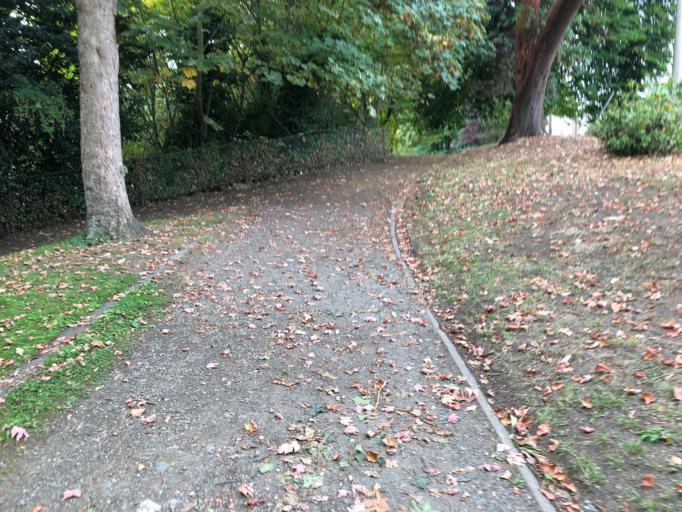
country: US
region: Washington
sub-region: King County
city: Seattle
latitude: 47.6271
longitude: -122.3648
